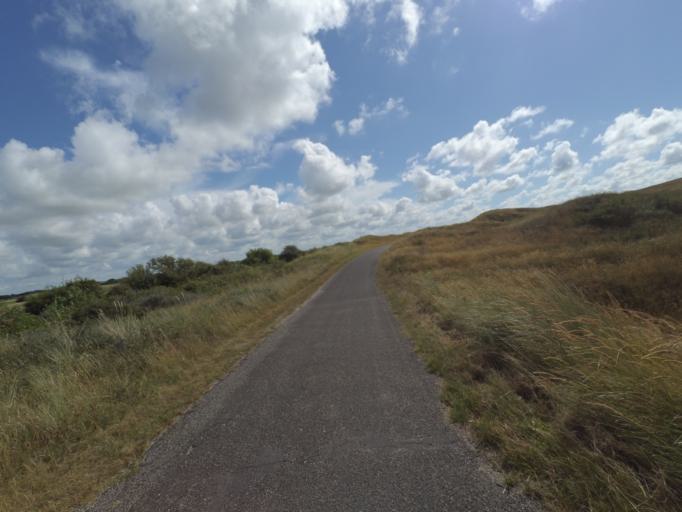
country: NL
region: North Holland
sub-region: Gemeente Texel
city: Den Burg
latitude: 53.1545
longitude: 4.8418
